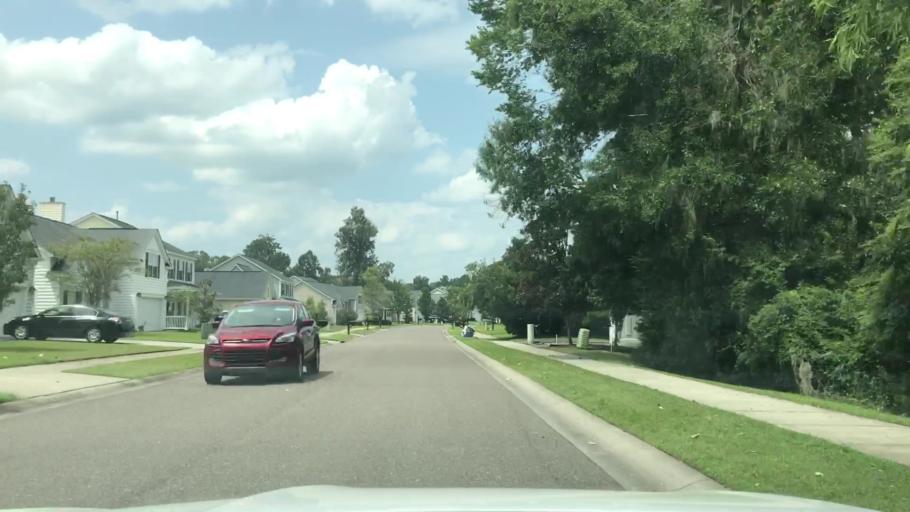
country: US
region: South Carolina
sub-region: Charleston County
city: Shell Point
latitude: 32.8316
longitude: -80.0970
